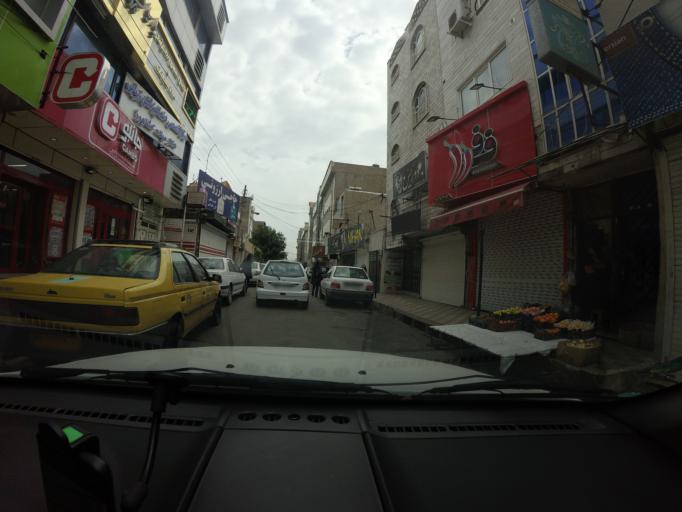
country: IR
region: Tehran
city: Eslamshahr
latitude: 35.5574
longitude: 51.2468
